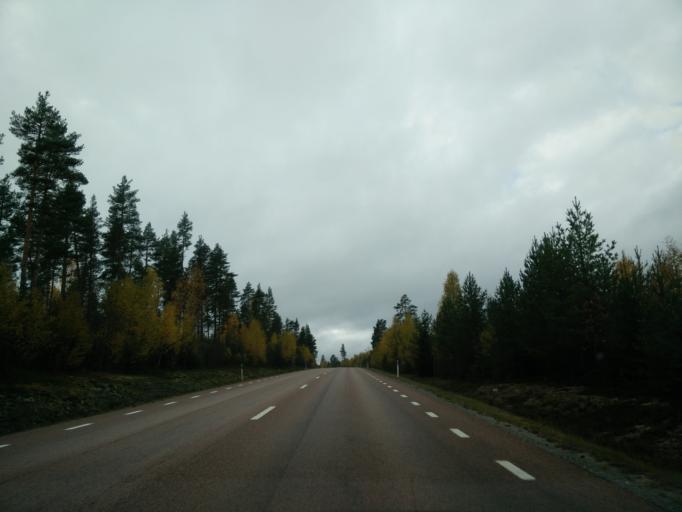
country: SE
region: Vaesternorrland
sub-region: Ange Kommun
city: Ange
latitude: 62.4915
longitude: 15.5039
